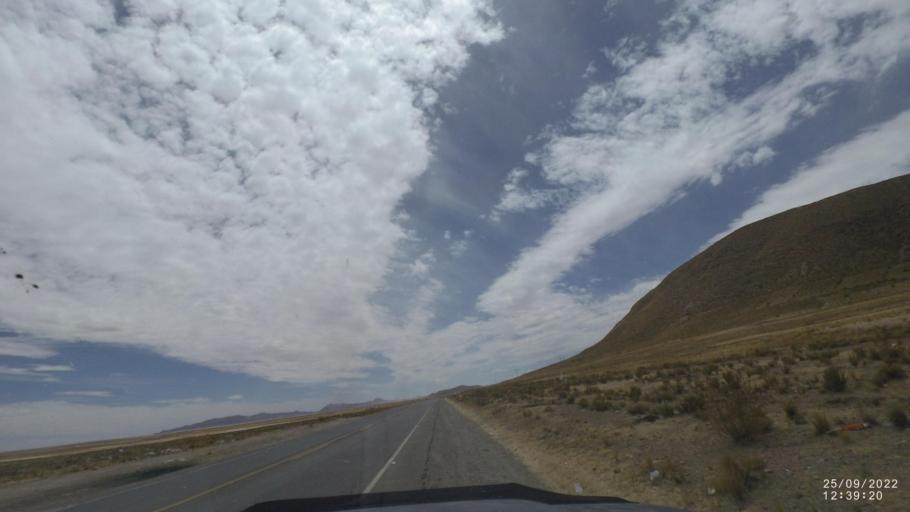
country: BO
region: Oruro
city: Machacamarca
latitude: -18.1246
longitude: -67.0028
